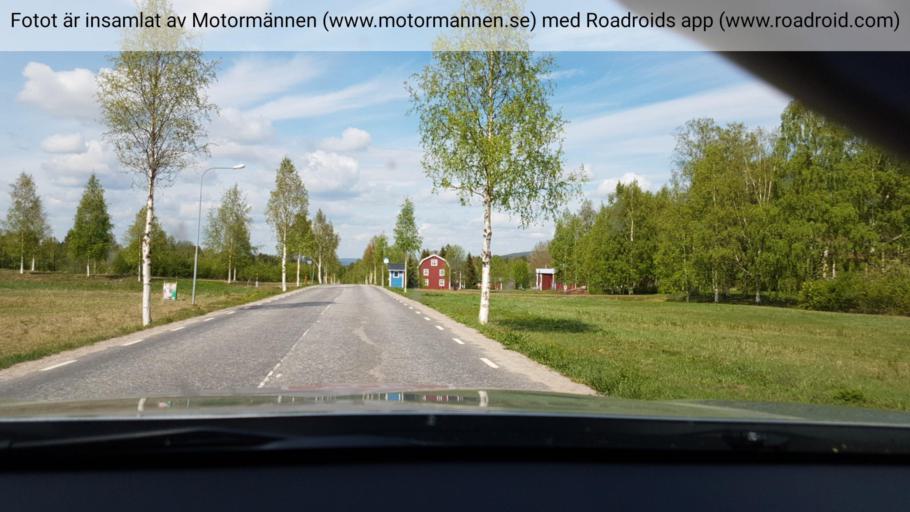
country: SE
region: Vaesterbotten
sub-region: Vannas Kommun
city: Vannasby
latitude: 63.8736
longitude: 19.8947
